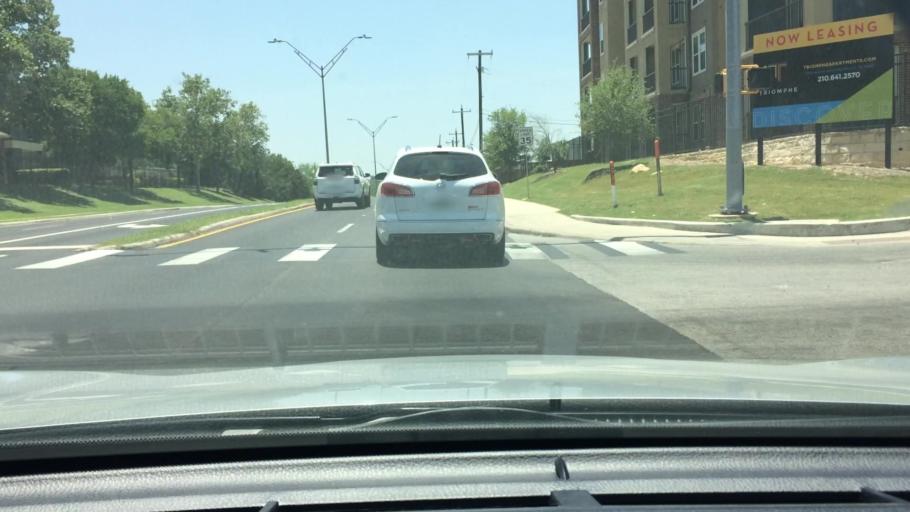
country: US
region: Texas
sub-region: Bexar County
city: Shavano Park
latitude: 29.5543
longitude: -98.5736
